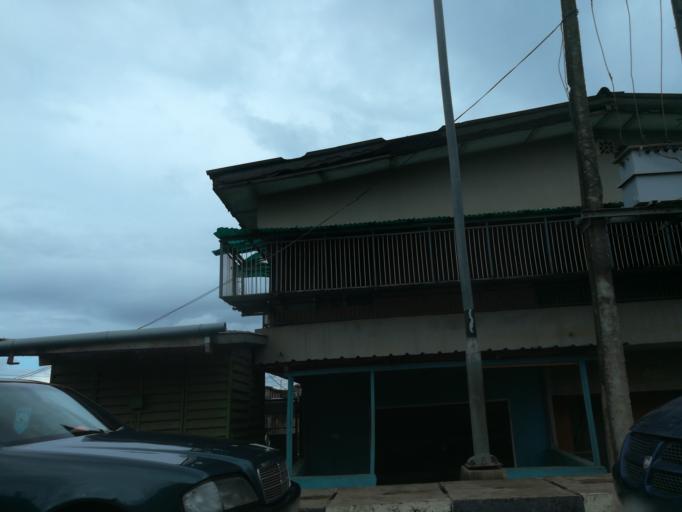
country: NG
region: Lagos
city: Agege
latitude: 6.6133
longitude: 3.3066
